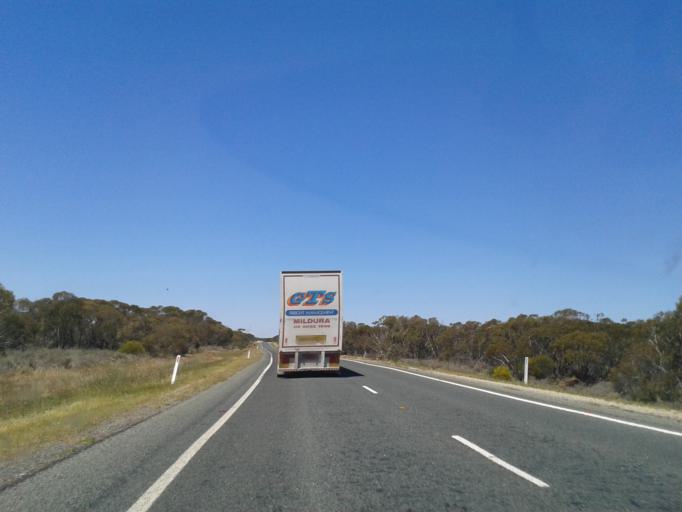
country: AU
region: New South Wales
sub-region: Wentworth
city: Gol Gol
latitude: -34.5030
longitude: 142.5795
